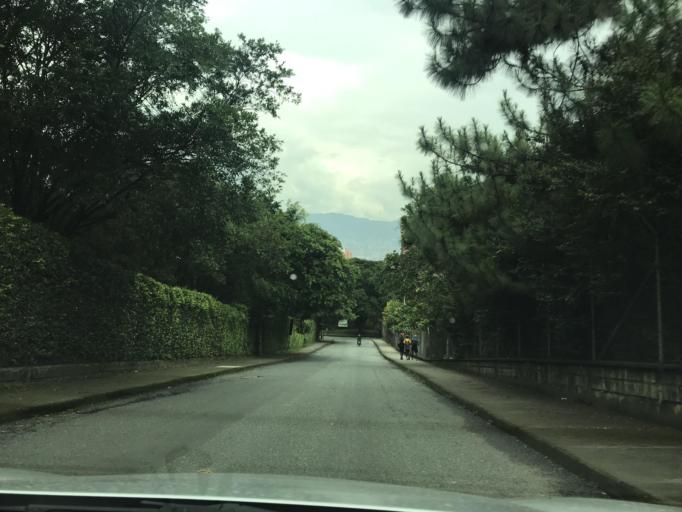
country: CO
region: Antioquia
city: Medellin
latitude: 6.2676
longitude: -75.6037
